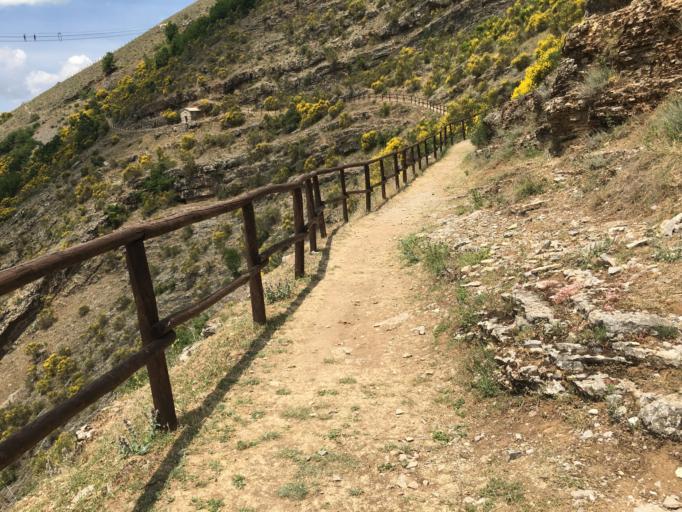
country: IT
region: Basilicate
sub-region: Provincia di Potenza
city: Sasso di Castalda
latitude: 40.4912
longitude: 15.6755
